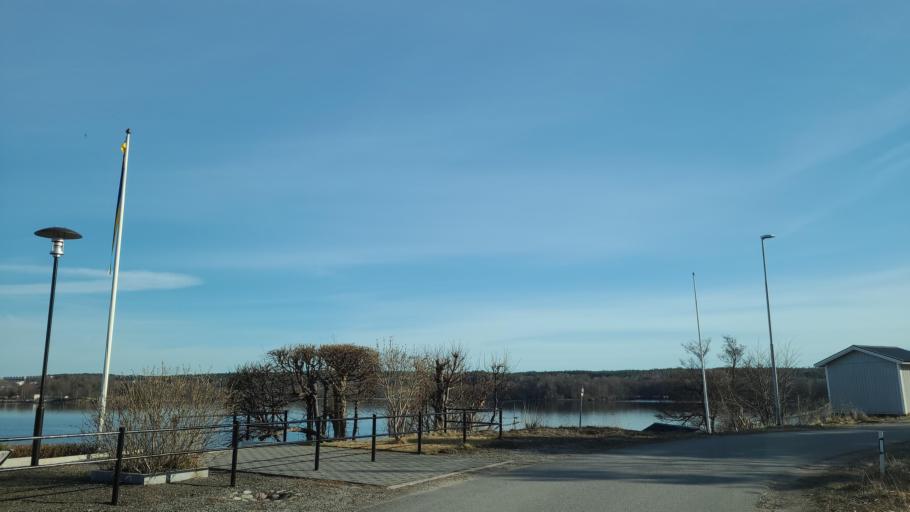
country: SE
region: Stockholm
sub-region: Ekero Kommun
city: Ekeroe
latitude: 59.2637
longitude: 17.7786
